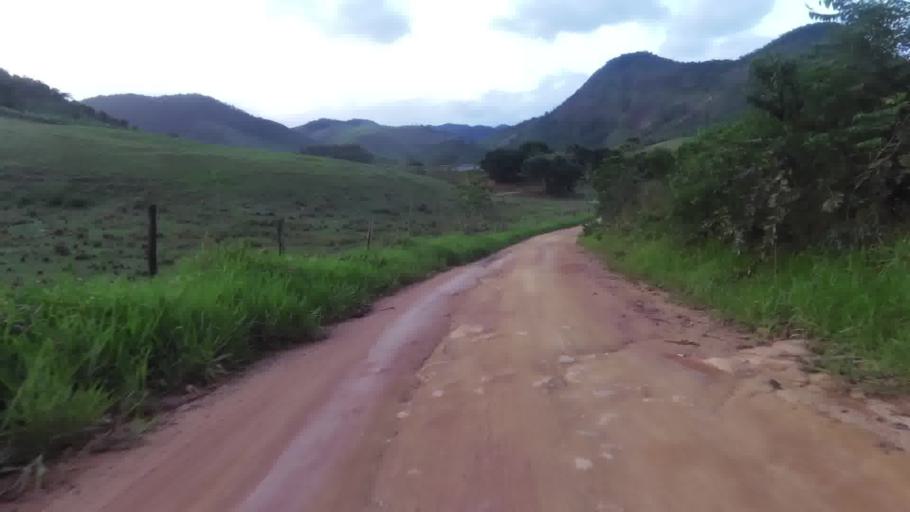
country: BR
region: Espirito Santo
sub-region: Guarapari
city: Guarapari
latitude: -20.6662
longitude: -40.6090
